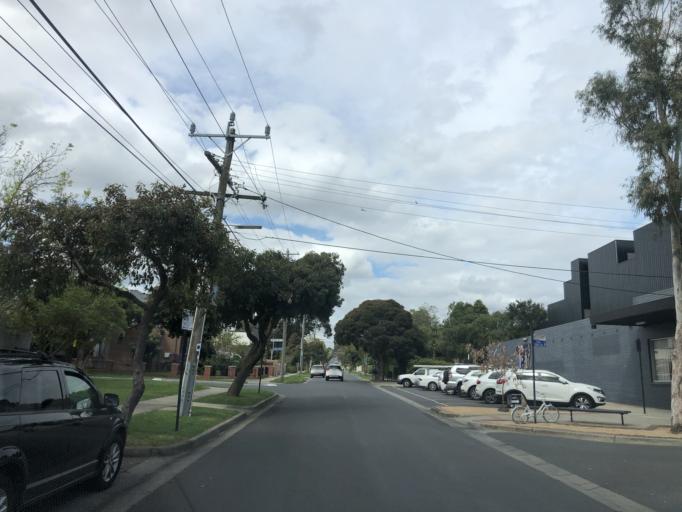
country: AU
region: Victoria
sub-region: Monash
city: Ashwood
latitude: -37.8603
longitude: 145.1067
